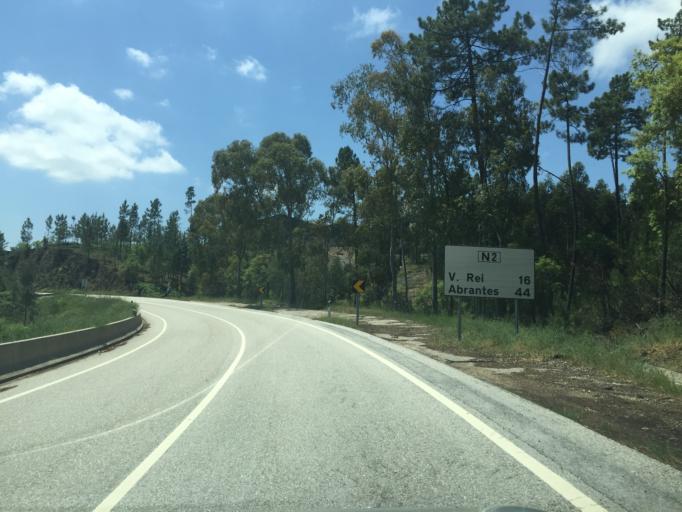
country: PT
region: Castelo Branco
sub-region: Serta
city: Serta
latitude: 39.7725
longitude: -8.1105
